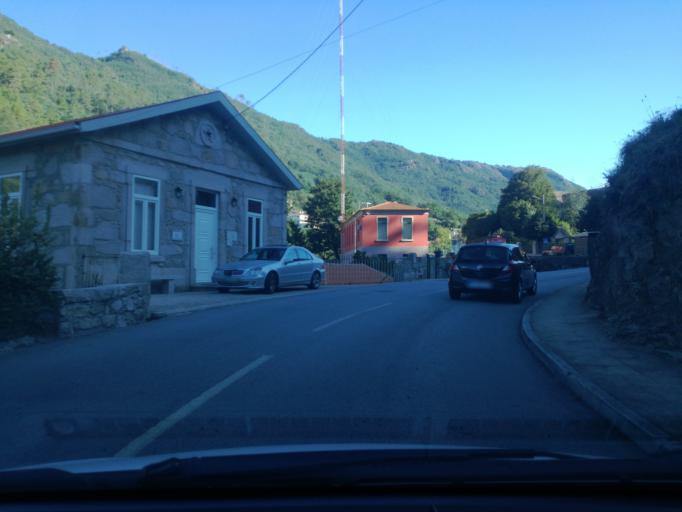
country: PT
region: Braga
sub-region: Vieira do Minho
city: Real
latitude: 41.7227
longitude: -8.1632
